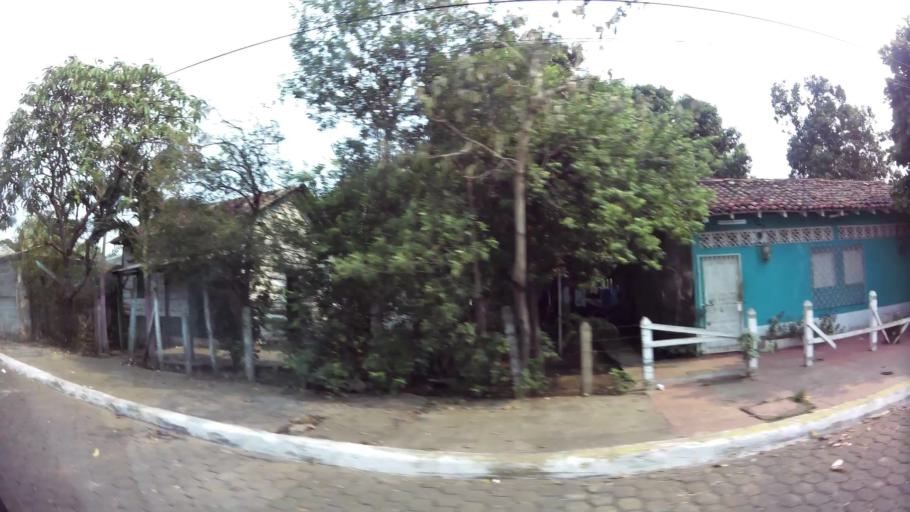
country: NI
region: Chinandega
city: Chinandega
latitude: 12.6283
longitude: -87.1245
